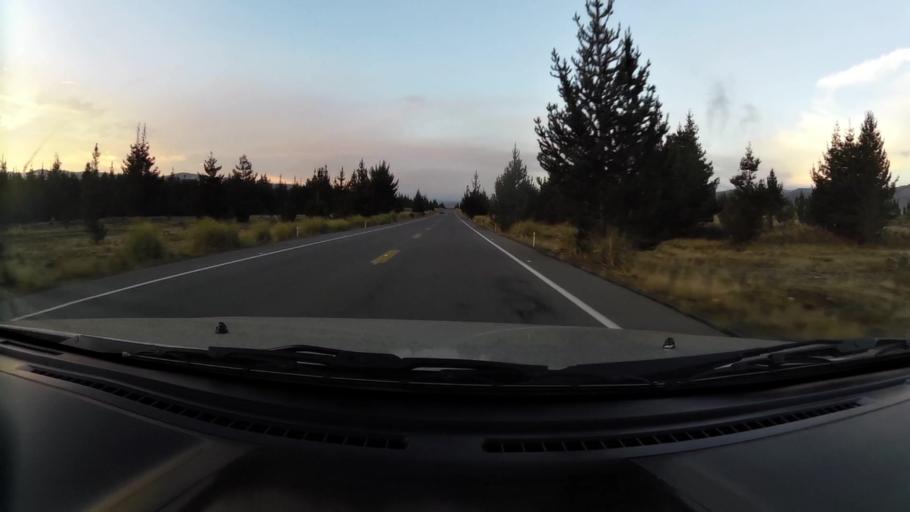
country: EC
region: Chimborazo
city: Alausi
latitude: -2.0332
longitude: -78.7358
